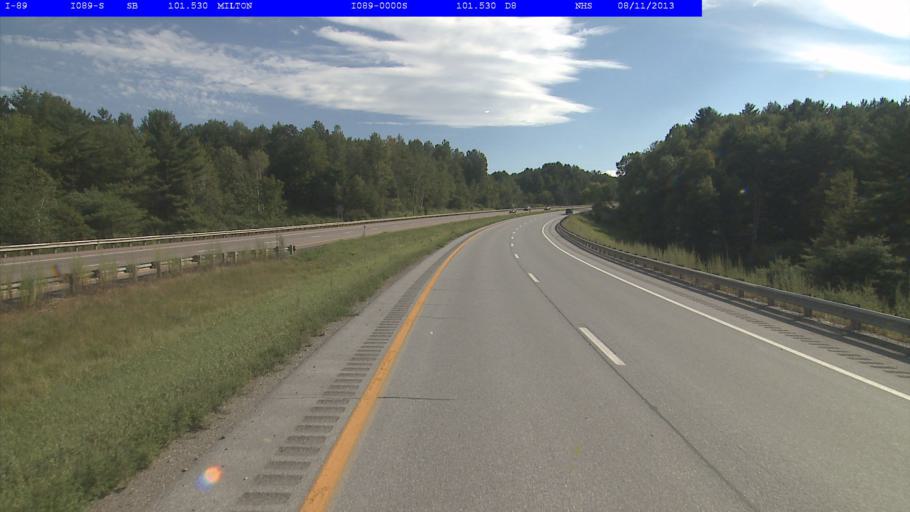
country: US
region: Vermont
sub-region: Chittenden County
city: Milton
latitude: 44.6353
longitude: -73.1412
